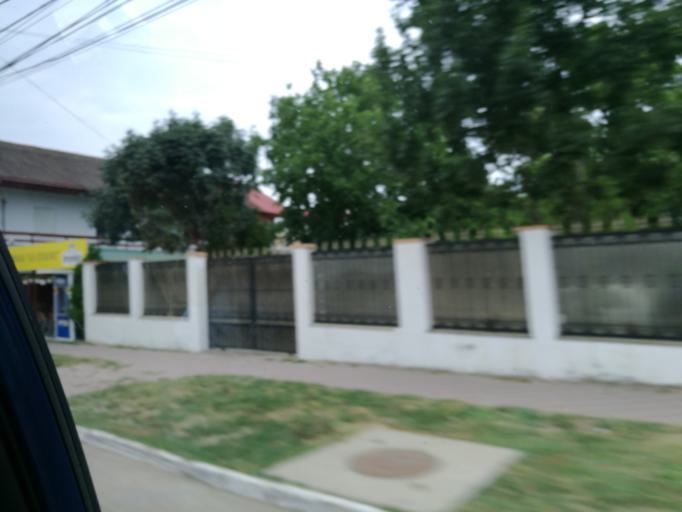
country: RO
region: Constanta
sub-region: Municipiul Mangalia
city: Mangalia
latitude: 43.7845
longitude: 28.5782
